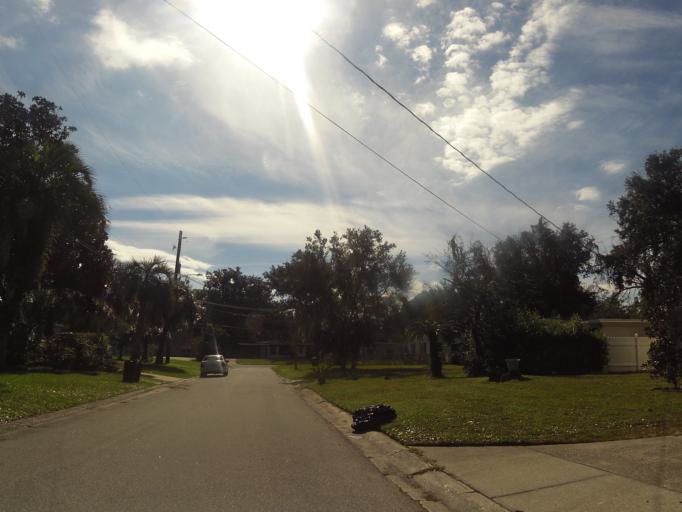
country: US
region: Florida
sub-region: Duval County
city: Jacksonville
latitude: 30.2595
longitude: -81.6377
